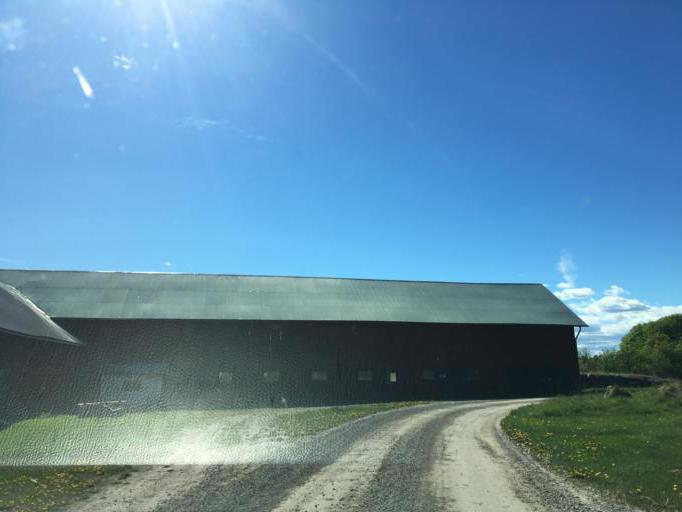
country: SE
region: Soedermanland
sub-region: Eskilstuna Kommun
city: Kvicksund
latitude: 59.3415
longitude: 16.2973
